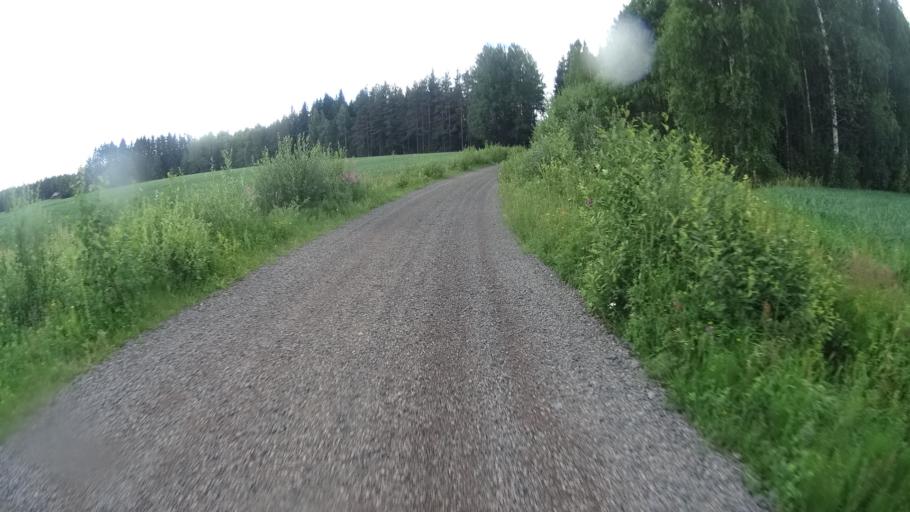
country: FI
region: Uusimaa
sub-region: Helsinki
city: Karkkila
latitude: 60.5944
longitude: 24.1634
